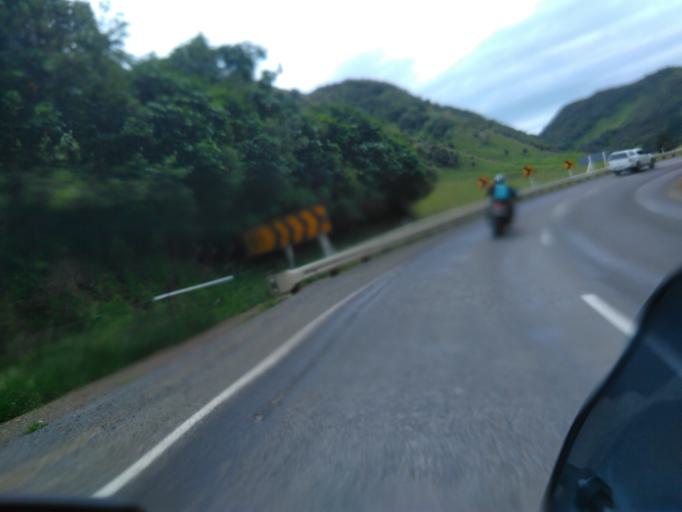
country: NZ
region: Bay of Plenty
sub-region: Opotiki District
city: Opotiki
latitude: -38.3777
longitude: 177.4795
